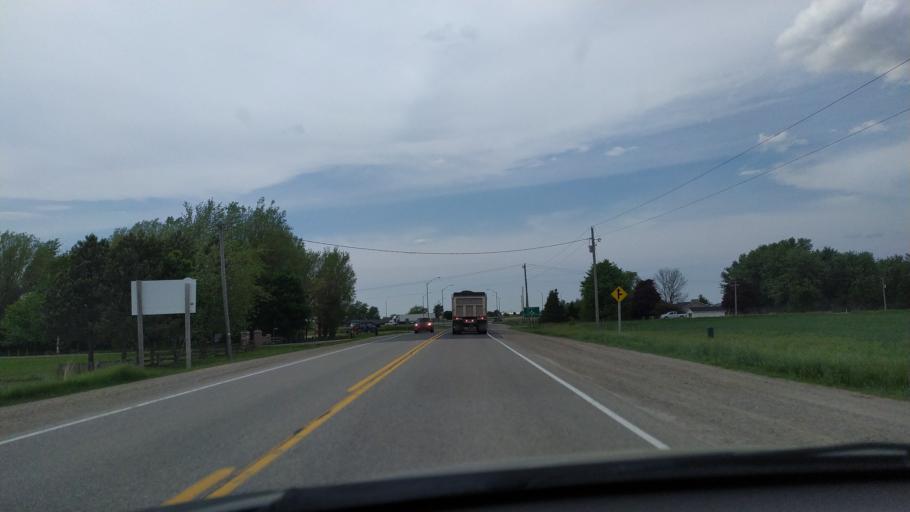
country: CA
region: Ontario
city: Stratford
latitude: 43.2452
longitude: -81.0837
